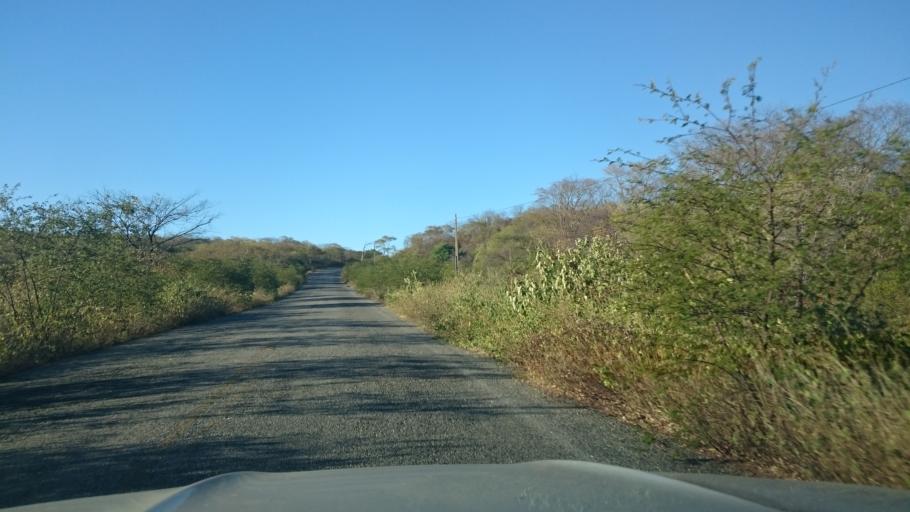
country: BR
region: Rio Grande do Norte
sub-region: Umarizal
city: Umarizal
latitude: -6.0186
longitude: -37.9082
